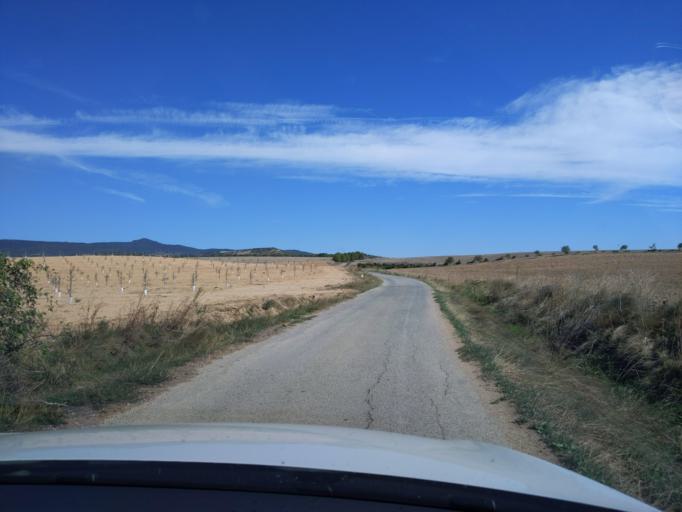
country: ES
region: Navarre
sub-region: Provincia de Navarra
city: Arroniz
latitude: 42.5592
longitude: -2.0677
